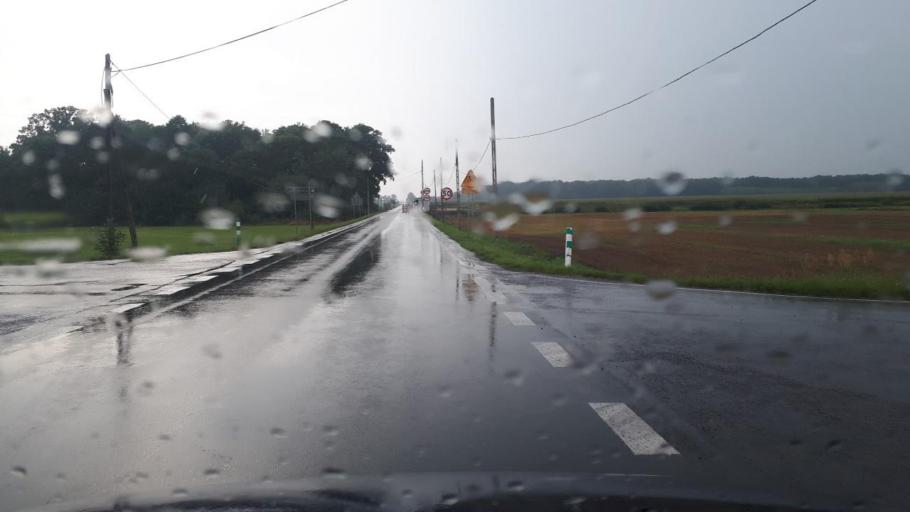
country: PL
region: Silesian Voivodeship
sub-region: Powiat gliwicki
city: Wielowies
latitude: 50.5280
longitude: 18.6407
